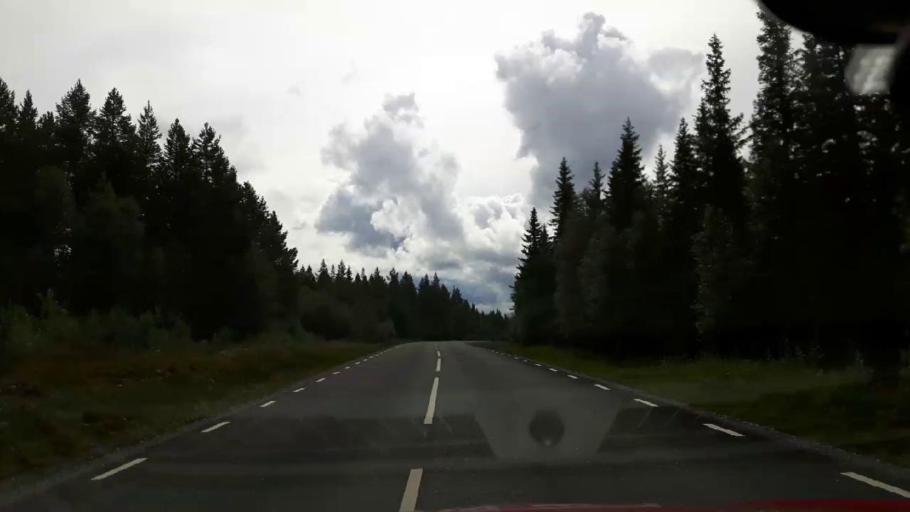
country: NO
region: Nord-Trondelag
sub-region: Lierne
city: Sandvika
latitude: 64.6237
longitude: 14.1223
